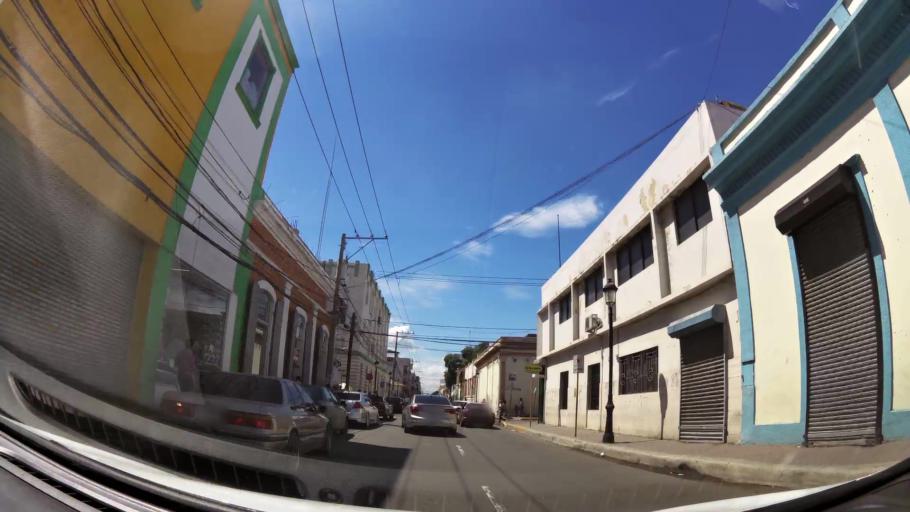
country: DO
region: Santiago
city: Santiago de los Caballeros
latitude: 19.4527
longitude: -70.7038
